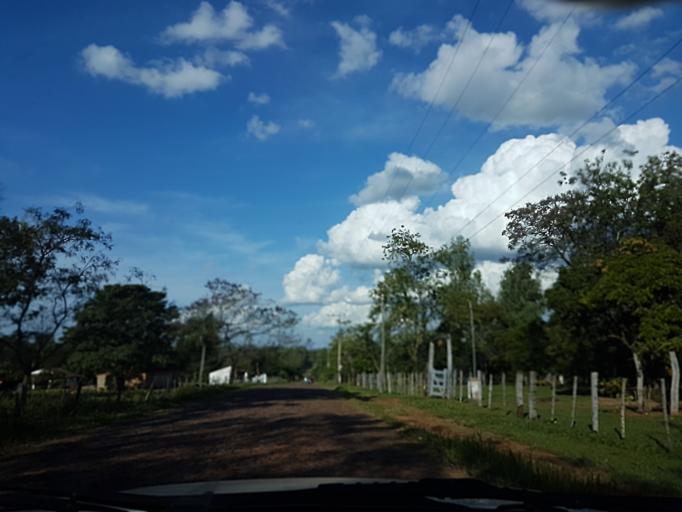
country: PY
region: Cordillera
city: Arroyos y Esteros
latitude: -24.9967
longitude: -57.1565
